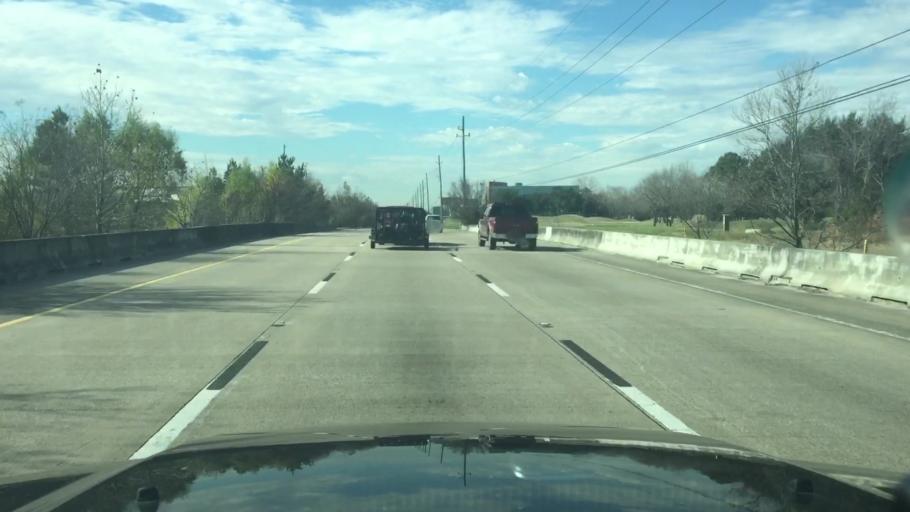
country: US
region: Texas
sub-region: Harris County
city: Hudson
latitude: 29.9343
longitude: -95.5346
